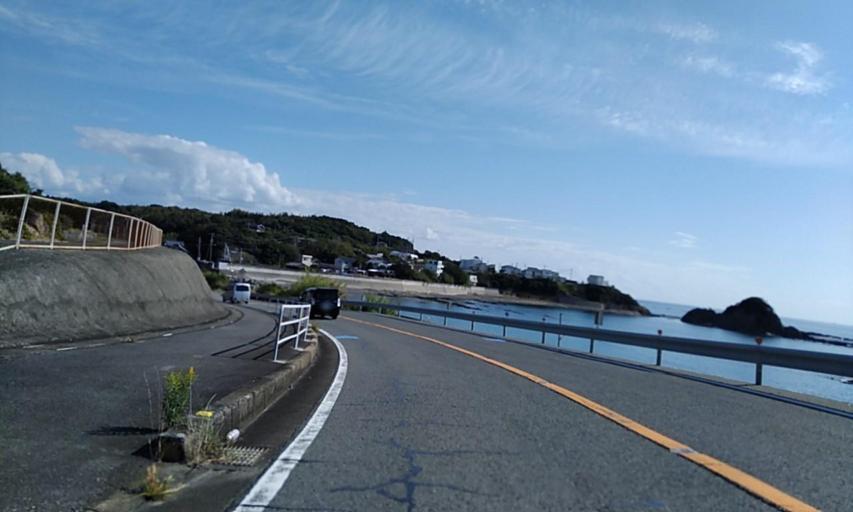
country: JP
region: Wakayama
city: Gobo
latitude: 33.8092
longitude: 135.2189
